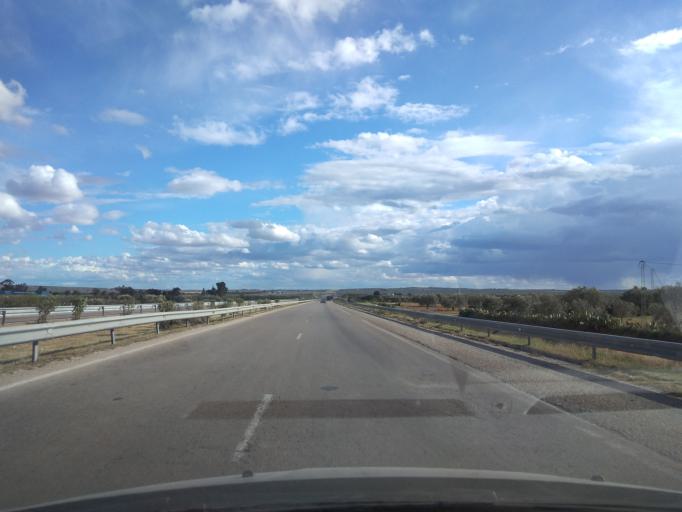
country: TN
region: Al Munastir
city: Manzil Kamil
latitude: 35.5901
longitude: 10.6051
